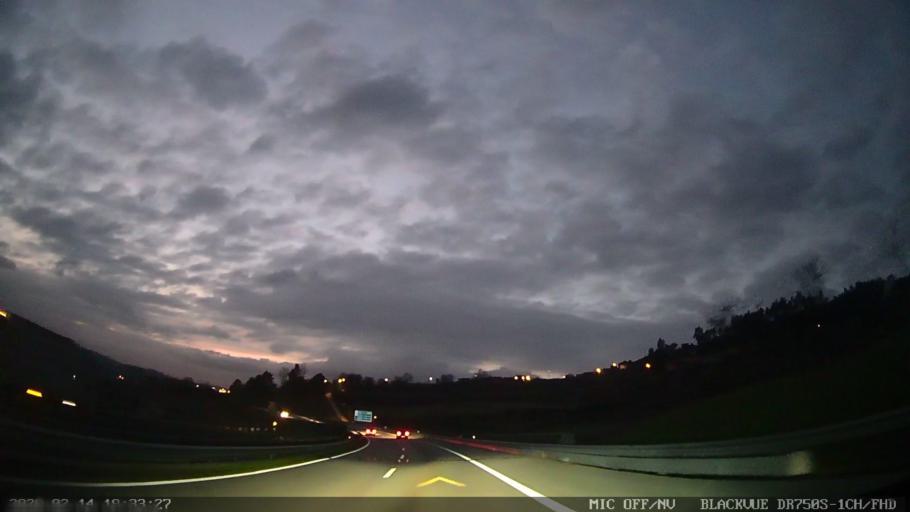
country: PT
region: Porto
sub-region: Marco de Canaveses
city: Marco de Canavezes
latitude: 41.2210
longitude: -8.1574
